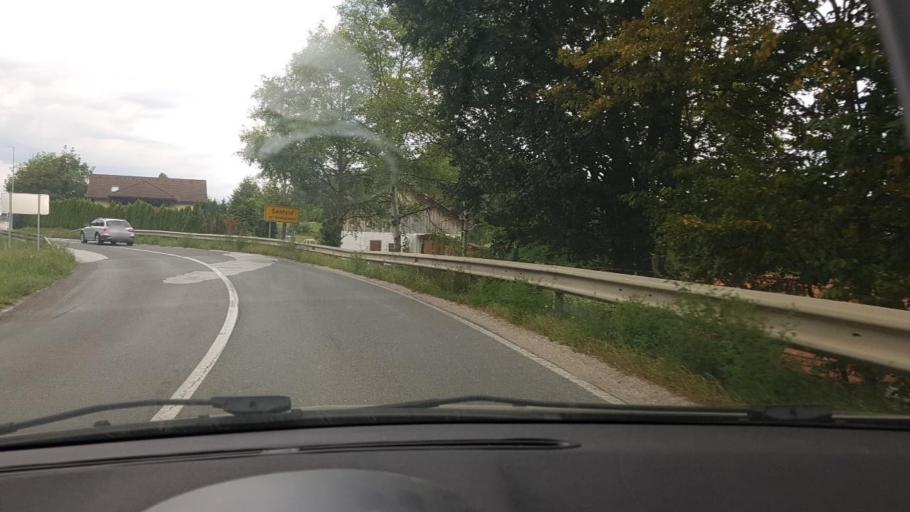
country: SI
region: Smarje pri Jelsah
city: Smarje pri Jelsah
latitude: 46.2279
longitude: 15.4734
